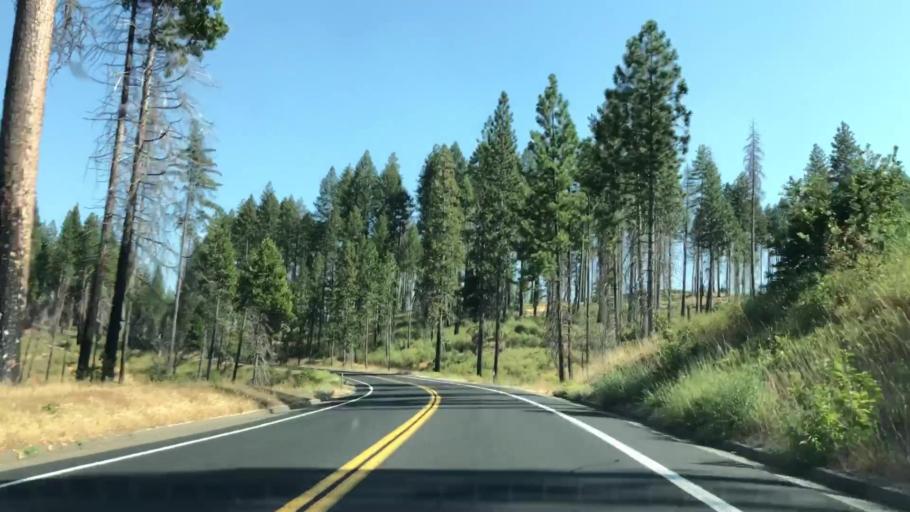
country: US
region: California
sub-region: Mariposa County
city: Midpines
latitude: 37.8258
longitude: -119.9730
